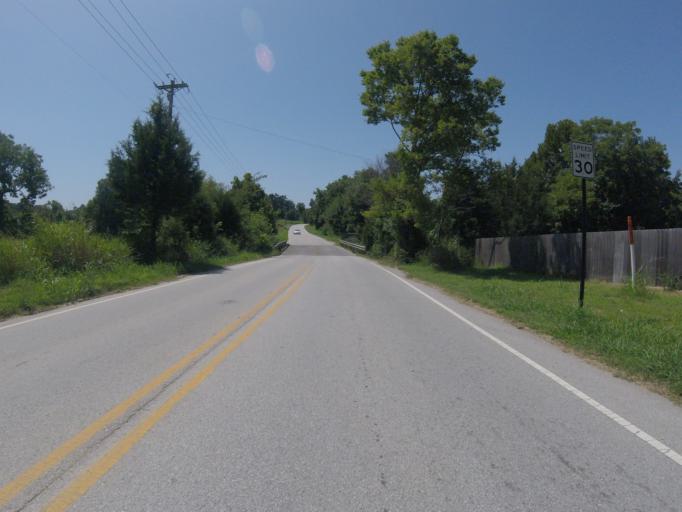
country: US
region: Arkansas
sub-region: Washington County
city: Farmington
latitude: 36.0922
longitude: -94.2150
